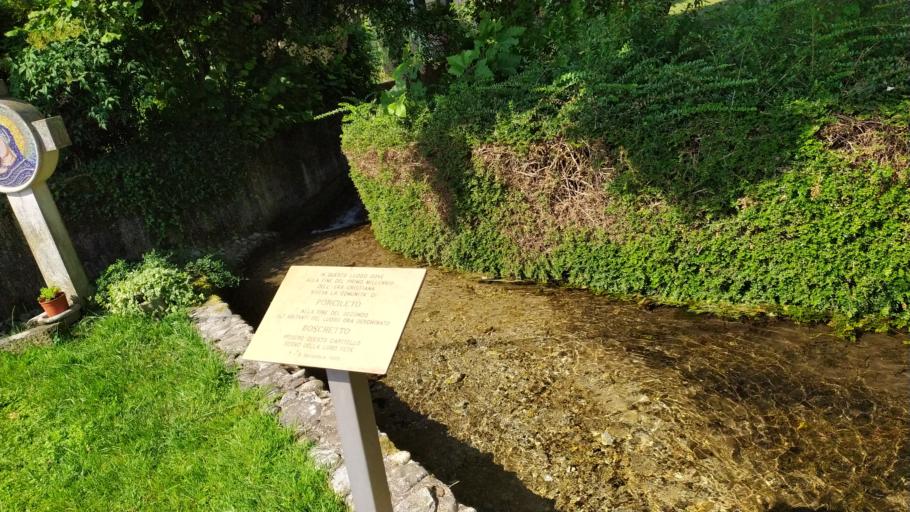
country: IT
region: Veneto
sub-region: Provincia di Vicenza
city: Novoledo
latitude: 45.6348
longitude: 11.5260
